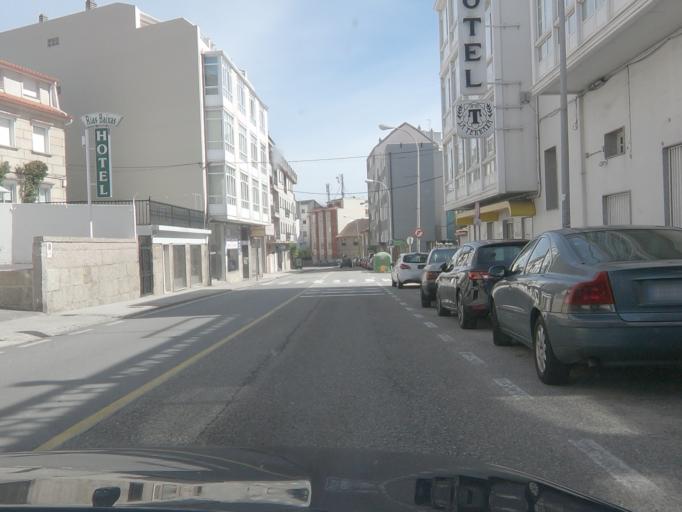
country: ES
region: Galicia
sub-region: Provincia de Pontevedra
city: Sanxenxo
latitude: 42.4027
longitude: -8.8087
